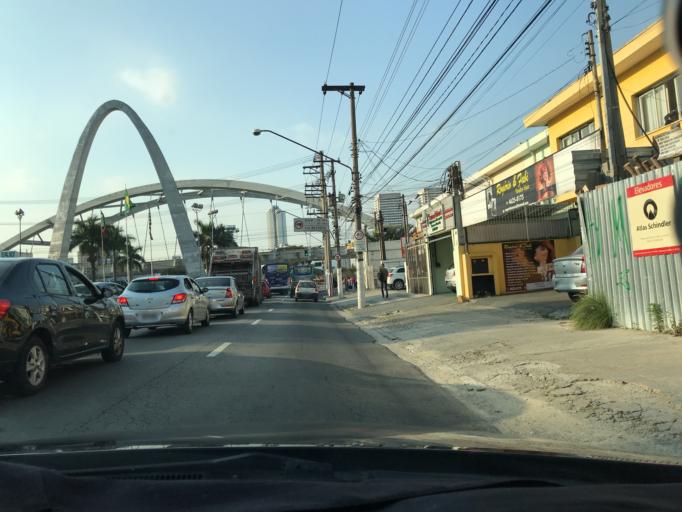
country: BR
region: Sao Paulo
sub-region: Osasco
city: Osasco
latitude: -23.5405
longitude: -46.7725
